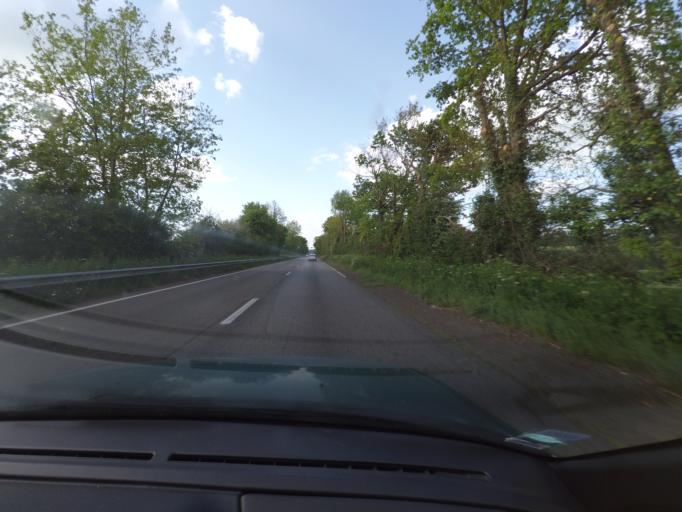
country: FR
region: Pays de la Loire
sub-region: Departement de la Vendee
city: Belleville-sur-Vie
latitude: 46.7602
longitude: -1.4306
